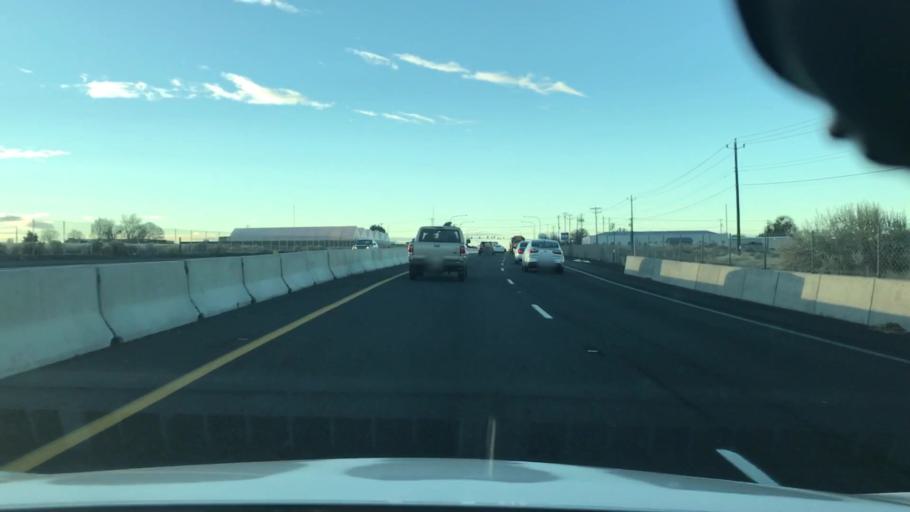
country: US
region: Washington
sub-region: Grant County
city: Moses Lake
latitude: 47.1348
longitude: -119.2569
